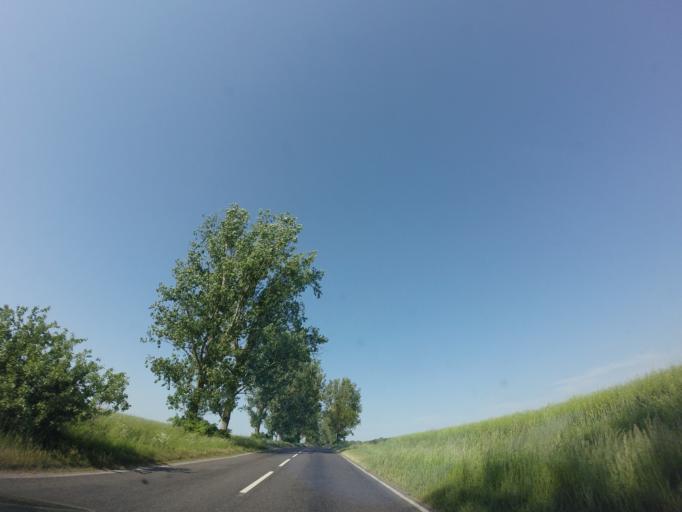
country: PL
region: West Pomeranian Voivodeship
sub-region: Powiat stargardzki
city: Kobylanka
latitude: 53.3146
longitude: 14.8444
